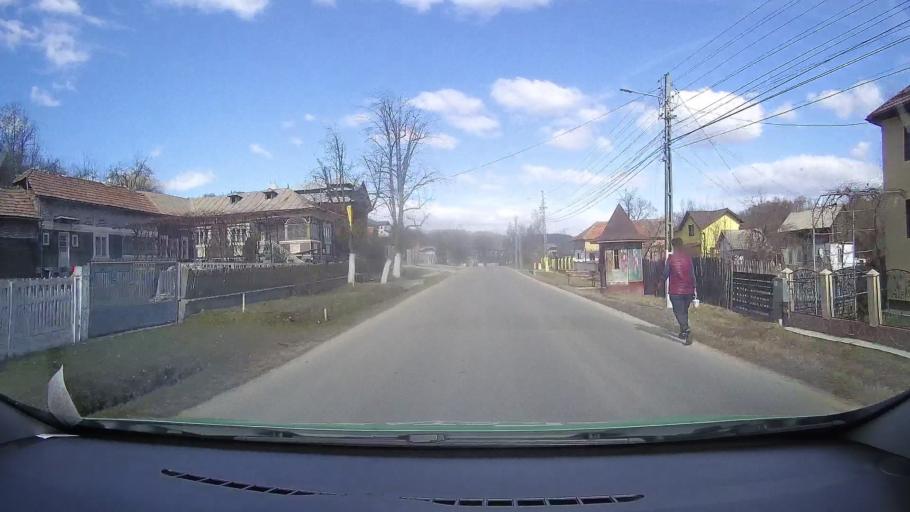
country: RO
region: Dambovita
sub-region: Comuna Vulcana Bai
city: Vulcana Bai
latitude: 45.0647
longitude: 25.3781
